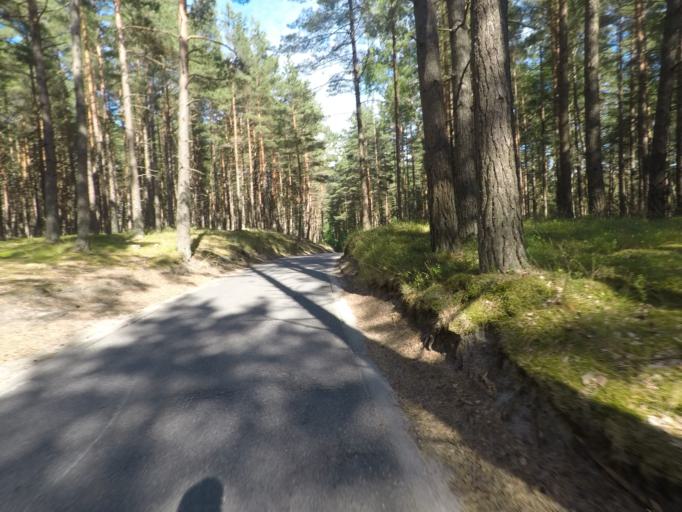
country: LT
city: Neringa
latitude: 55.5413
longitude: 21.1083
